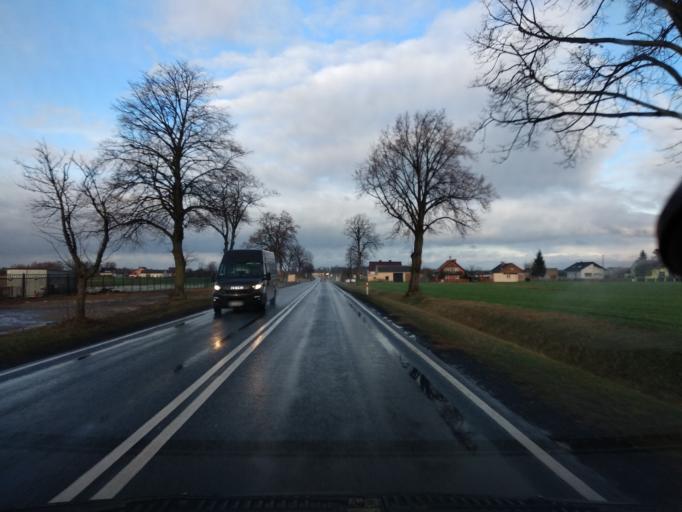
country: PL
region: Greater Poland Voivodeship
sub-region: Powiat koninski
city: Rychwal
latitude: 52.0551
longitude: 18.1632
